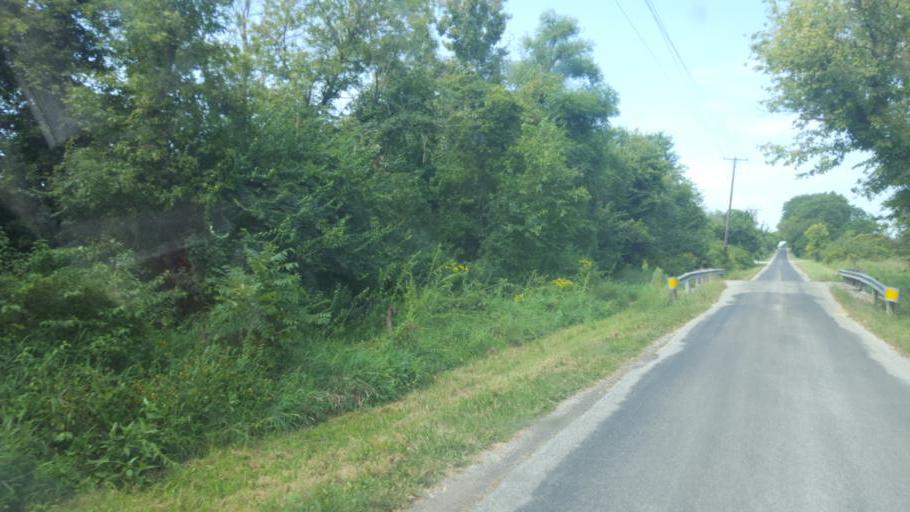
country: US
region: Ohio
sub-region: Delaware County
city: Ashley
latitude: 40.4502
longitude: -83.0489
